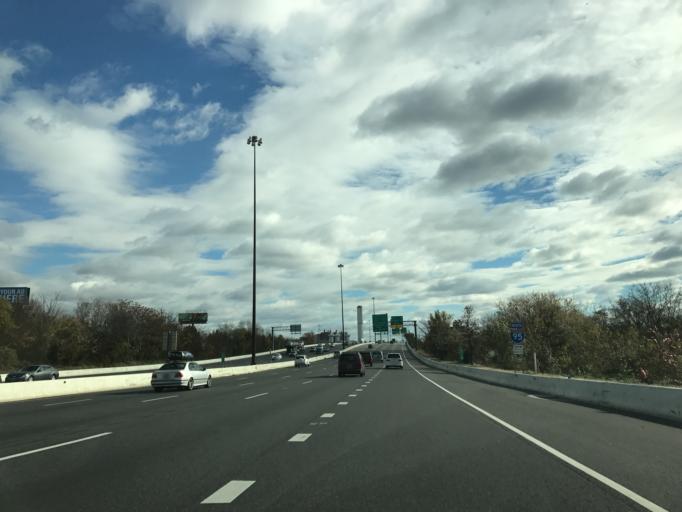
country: US
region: Maryland
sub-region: Baltimore County
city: Lansdowne
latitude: 39.2705
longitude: -76.6436
